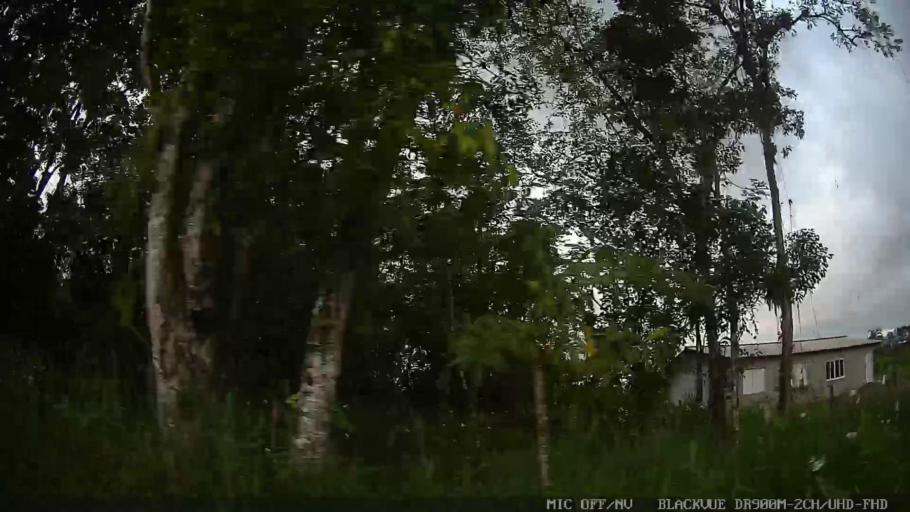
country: BR
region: Sao Paulo
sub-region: Itanhaem
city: Itanhaem
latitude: -24.1011
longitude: -46.8034
